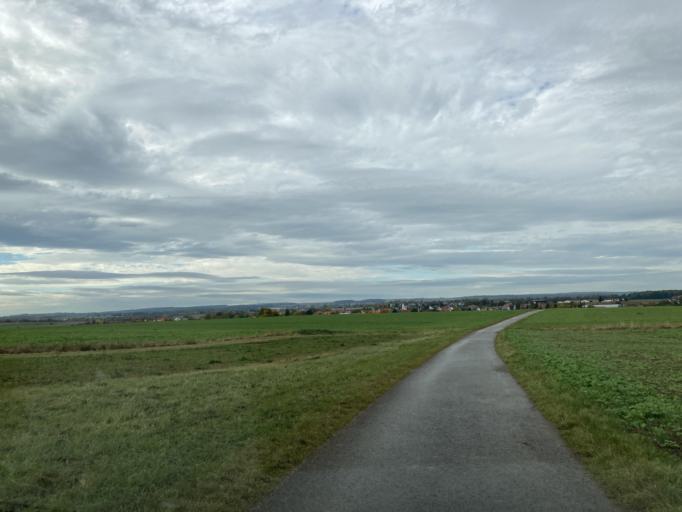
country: DE
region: Baden-Wuerttemberg
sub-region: Regierungsbezirk Stuttgart
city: Bondorf
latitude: 48.5210
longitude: 8.8797
